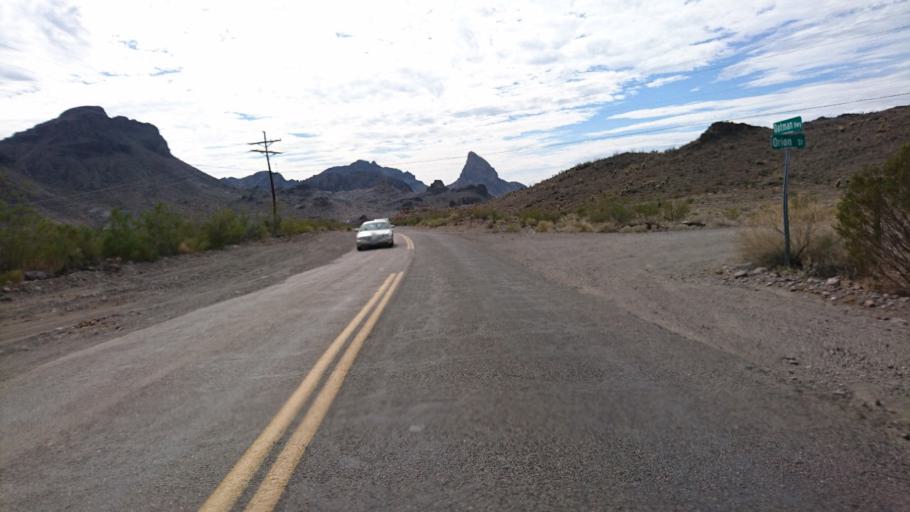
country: US
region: Arizona
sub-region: Mohave County
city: Mohave Valley
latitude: 35.0113
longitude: -114.3900
